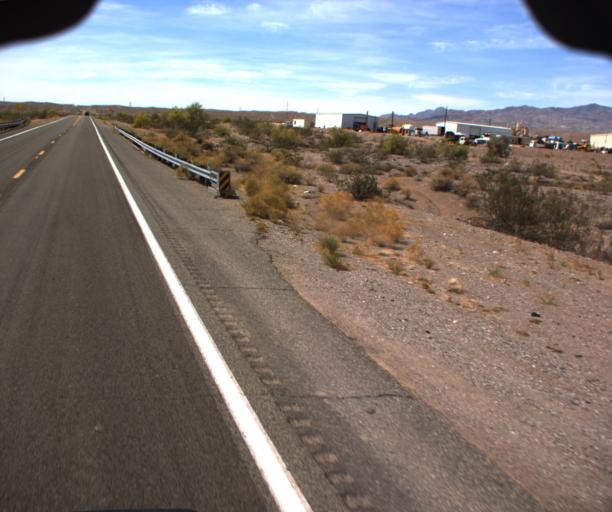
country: US
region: Arizona
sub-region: Mohave County
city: Lake Havasu City
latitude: 34.4134
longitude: -114.1929
